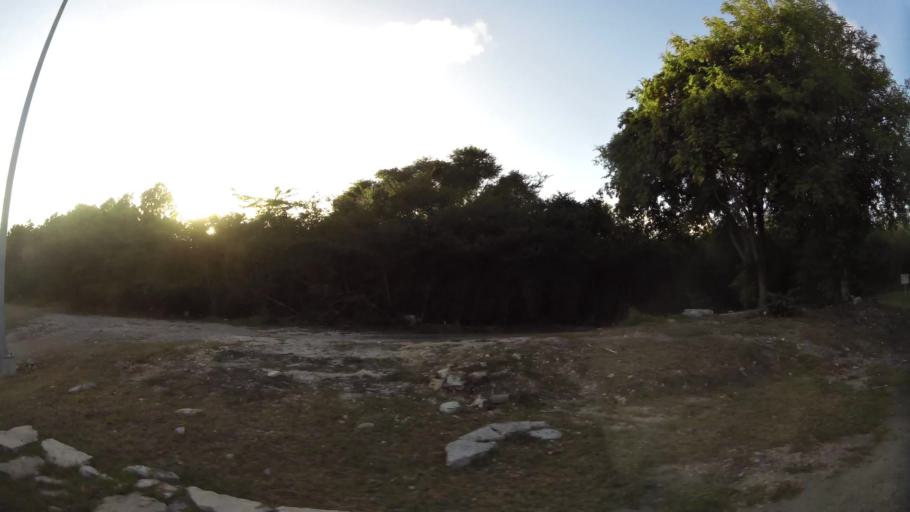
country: AG
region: Saint George
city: Piggotts
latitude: 17.1569
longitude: -61.7984
